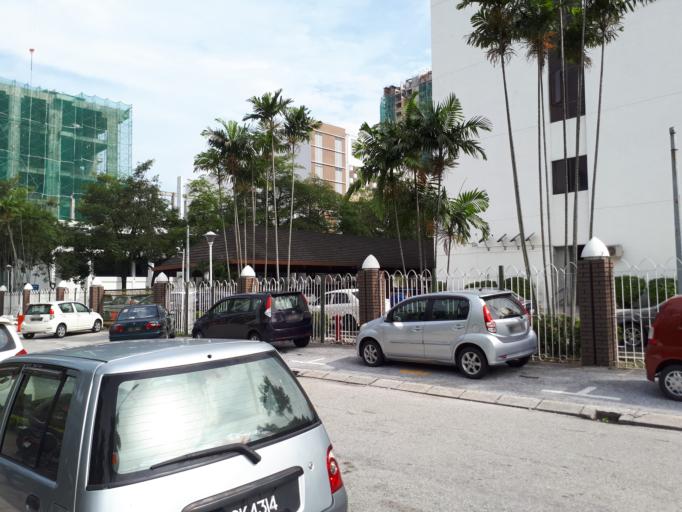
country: MY
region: Perak
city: Ipoh
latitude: 4.5979
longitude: 101.0902
